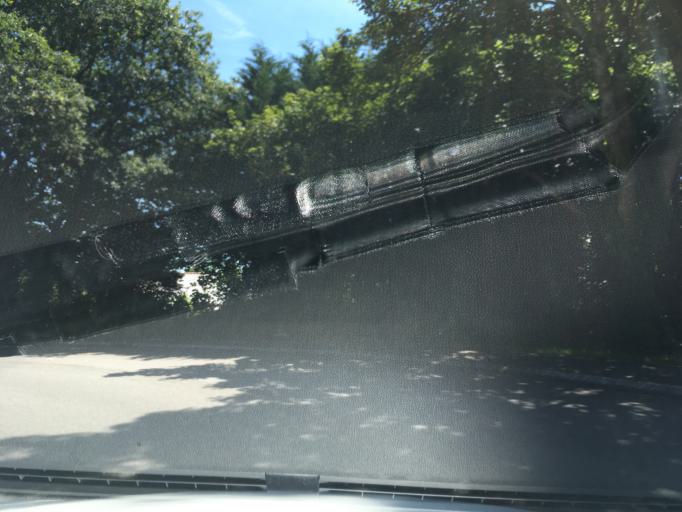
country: FR
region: Brittany
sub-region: Departement du Finistere
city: Quimper
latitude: 47.9922
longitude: -4.1382
